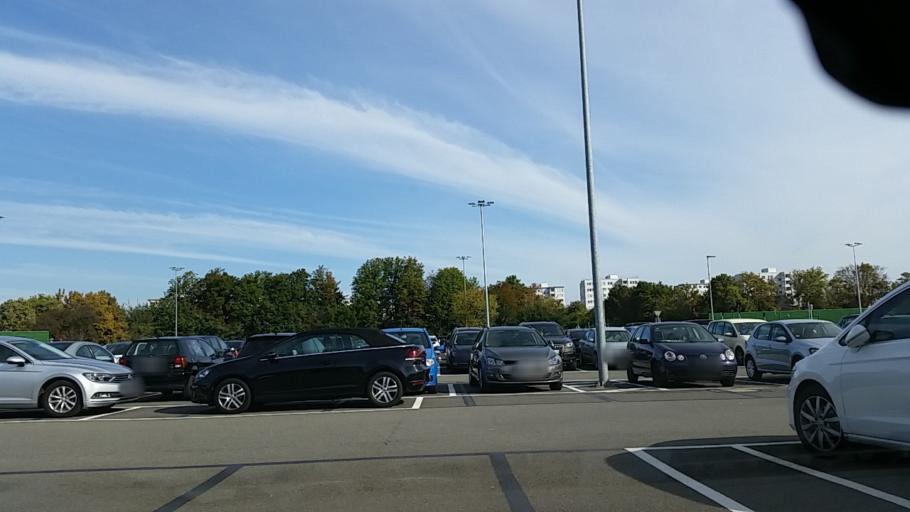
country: DE
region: Lower Saxony
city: Wolfsburg
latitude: 52.4426
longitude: 10.7831
